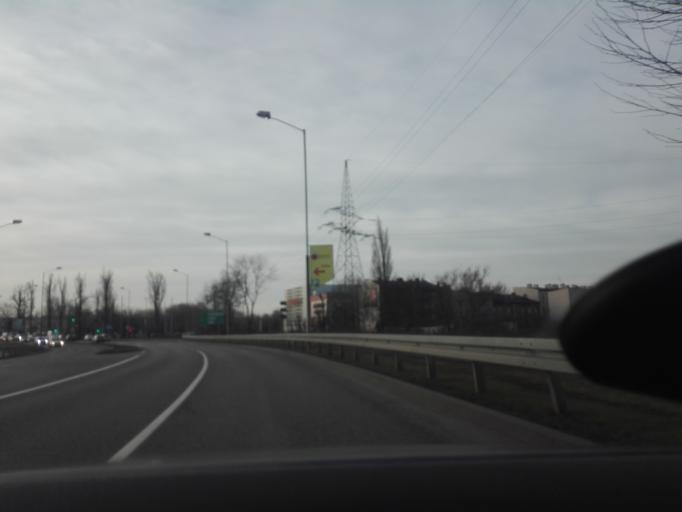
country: PL
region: Silesian Voivodeship
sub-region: Katowice
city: Katowice
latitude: 50.2640
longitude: 19.0086
